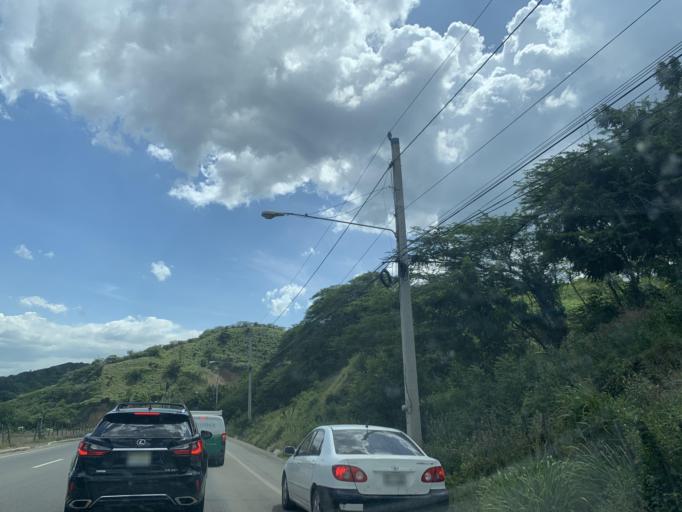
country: DO
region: Santiago
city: Villa Bisono
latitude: 19.5975
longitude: -70.8419
